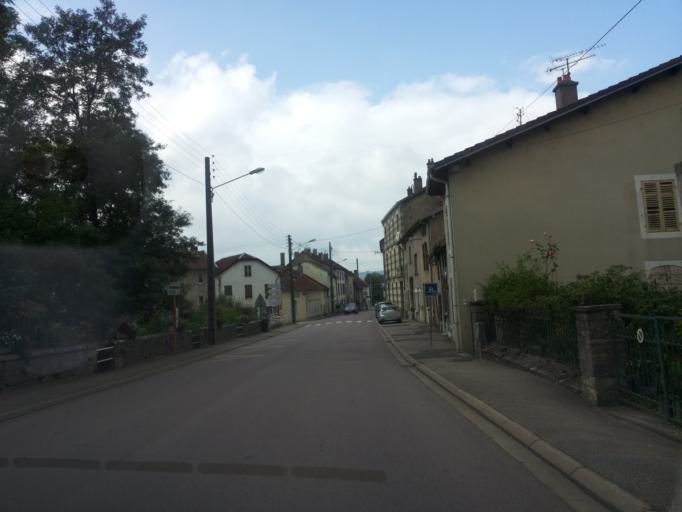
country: FR
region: Lorraine
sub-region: Departement des Vosges
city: Neufchateau
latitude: 48.3578
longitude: 5.6989
